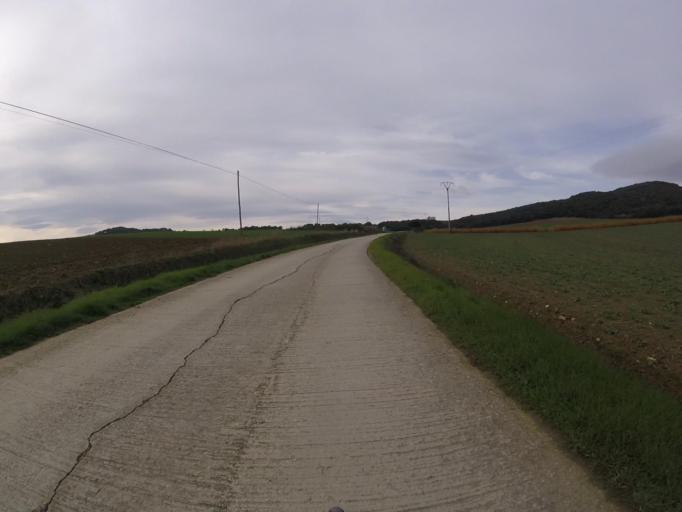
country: ES
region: Navarre
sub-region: Provincia de Navarra
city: Estella
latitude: 42.7192
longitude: -2.0376
